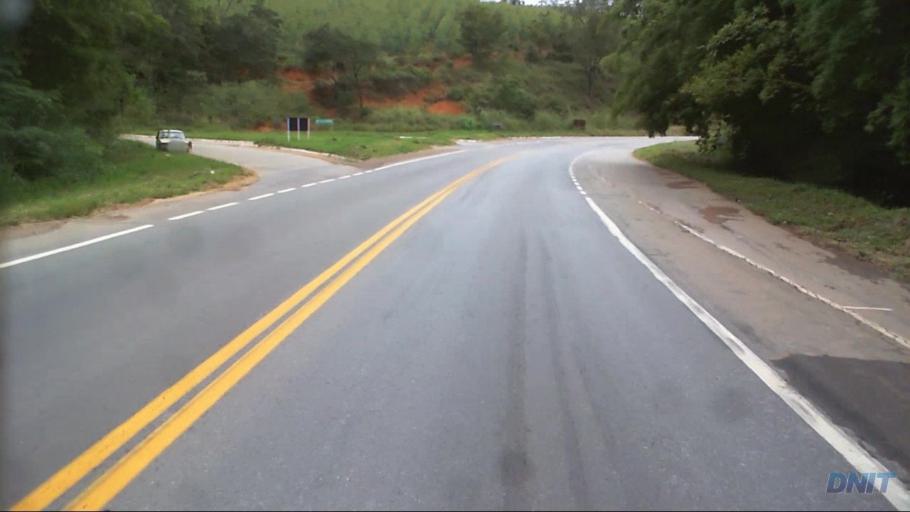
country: BR
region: Minas Gerais
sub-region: Joao Monlevade
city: Joao Monlevade
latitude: -19.8532
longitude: -43.2564
